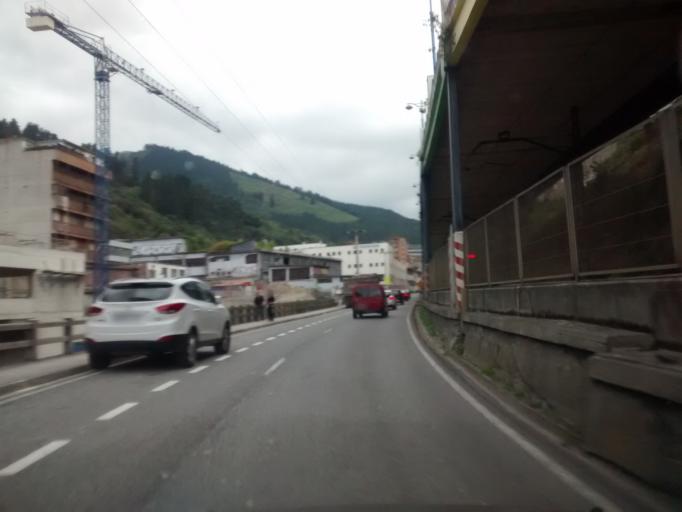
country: ES
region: Basque Country
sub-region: Provincia de Guipuzcoa
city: Eibar
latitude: 43.1827
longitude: -2.4827
